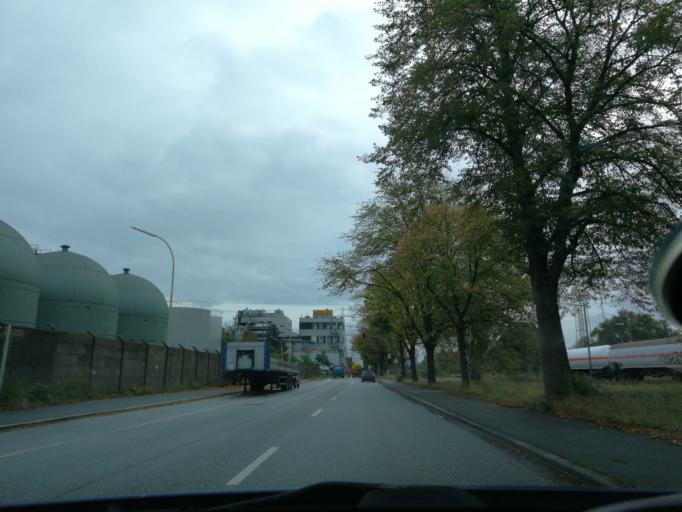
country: DE
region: Hamburg
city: Harburg
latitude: 53.4735
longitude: 9.9557
